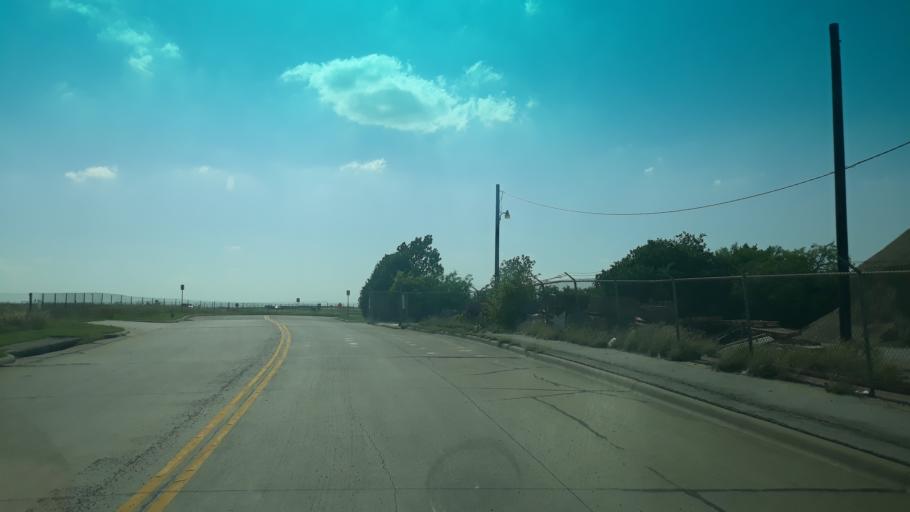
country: US
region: Texas
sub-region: Dallas County
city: Irving
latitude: 32.8705
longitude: -97.0056
